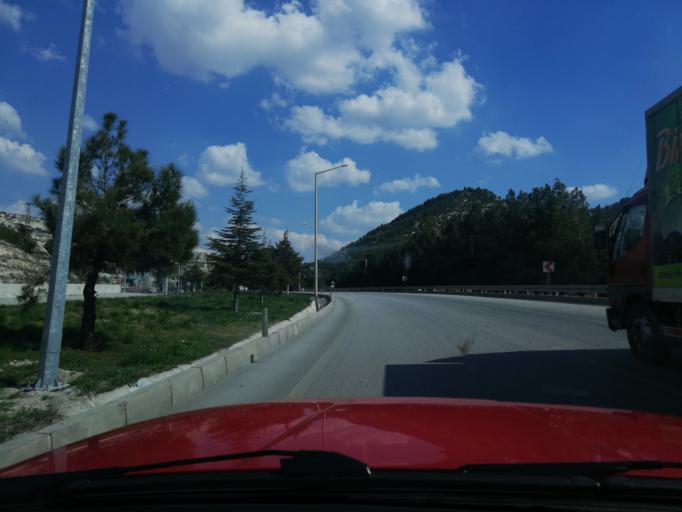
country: TR
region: Burdur
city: Burdur
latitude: 37.7091
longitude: 30.2961
